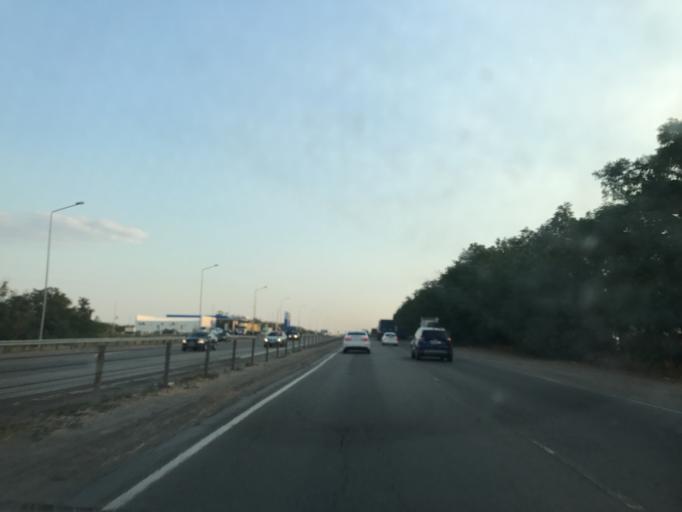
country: RU
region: Rostov
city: Likhoy
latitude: 48.1807
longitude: 40.2650
